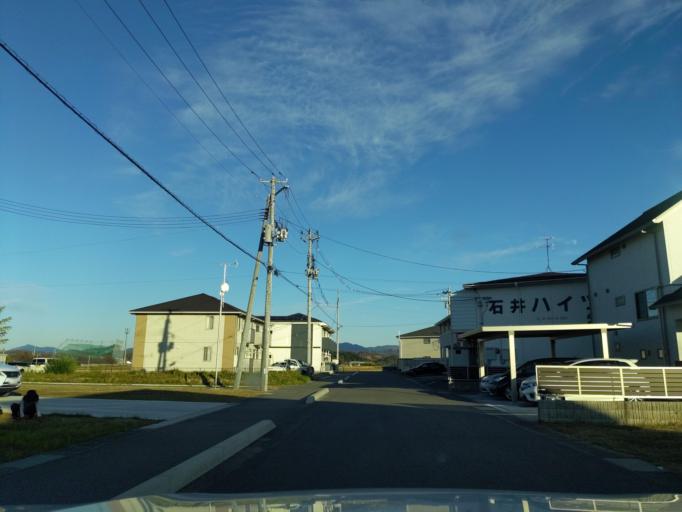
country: JP
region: Fukushima
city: Koriyama
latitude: 37.3556
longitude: 140.3828
